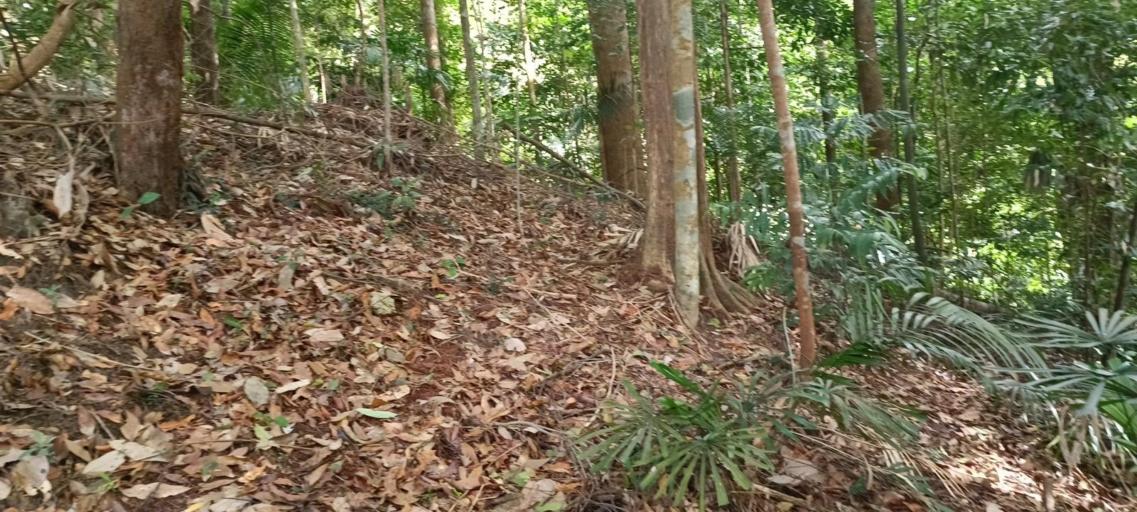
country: MY
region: Penang
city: Bukit Mertajam
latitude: 5.3624
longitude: 100.4826
